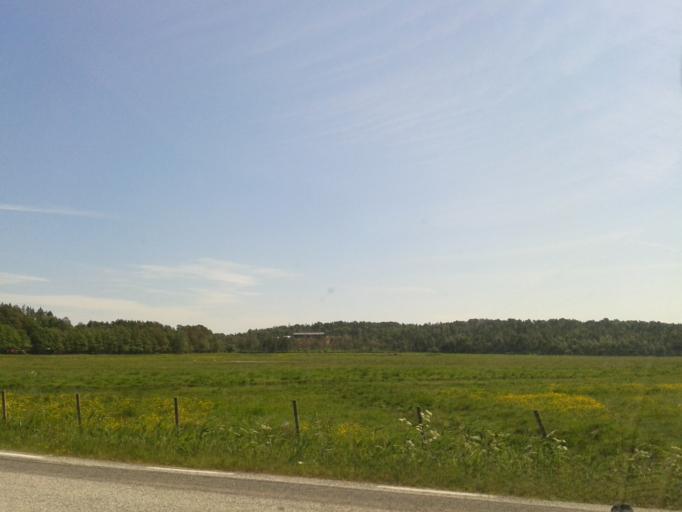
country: SE
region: Vaestra Goetaland
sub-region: Stromstads Kommun
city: Stroemstad
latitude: 58.8578
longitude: 11.2320
